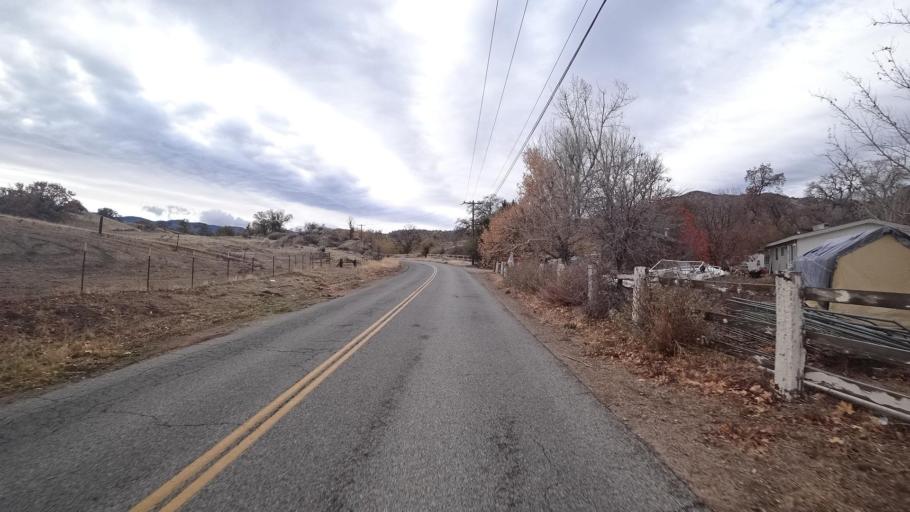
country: US
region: California
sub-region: Kern County
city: Golden Hills
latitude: 35.1395
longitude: -118.4997
